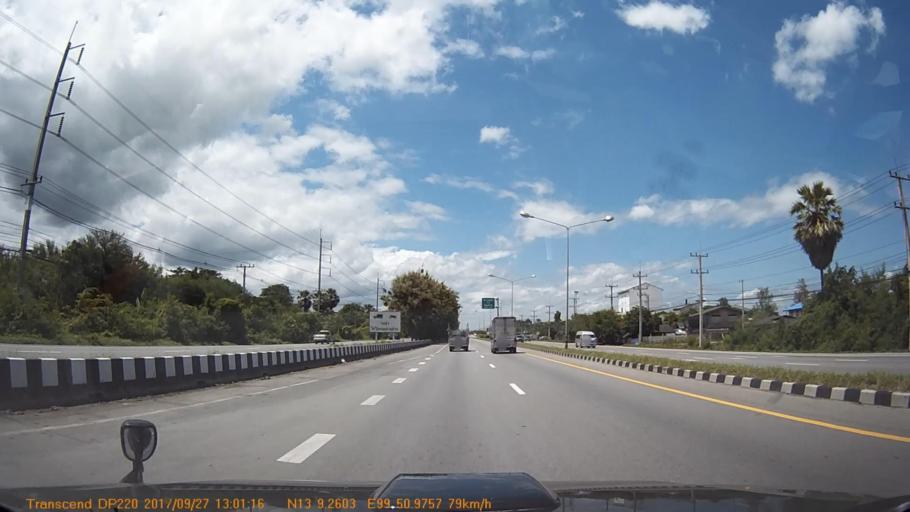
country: TH
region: Phetchaburi
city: Khao Yoi
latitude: 13.1544
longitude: 99.8496
